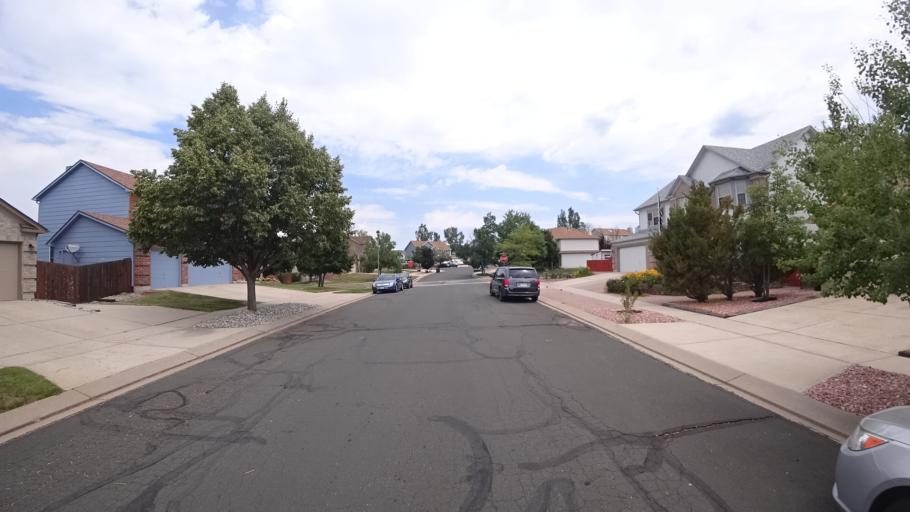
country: US
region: Colorado
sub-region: El Paso County
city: Black Forest
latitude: 38.9601
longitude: -104.7744
